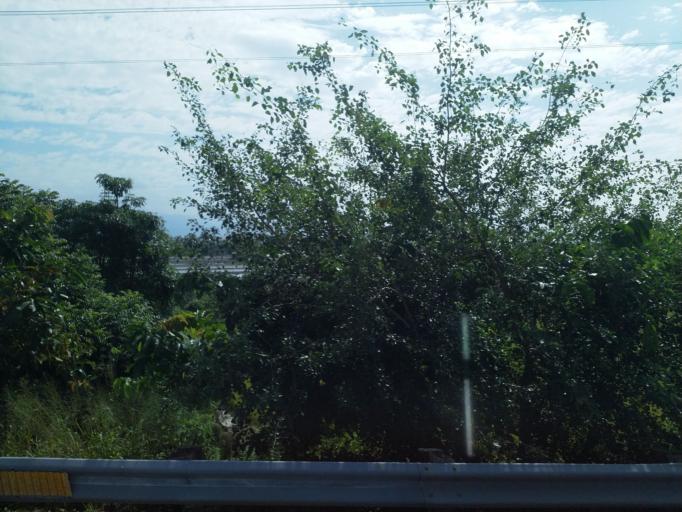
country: TW
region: Taiwan
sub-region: Pingtung
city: Pingtung
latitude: 22.8099
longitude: 120.4845
